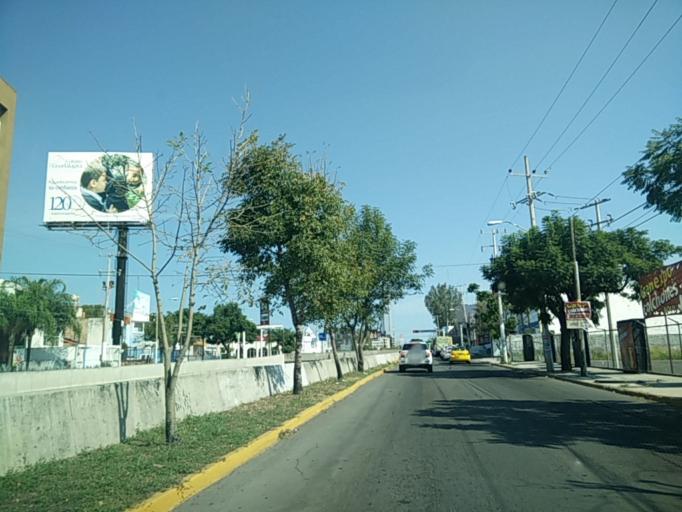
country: MX
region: Jalisco
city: Guadalajara
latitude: 20.6562
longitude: -103.3993
